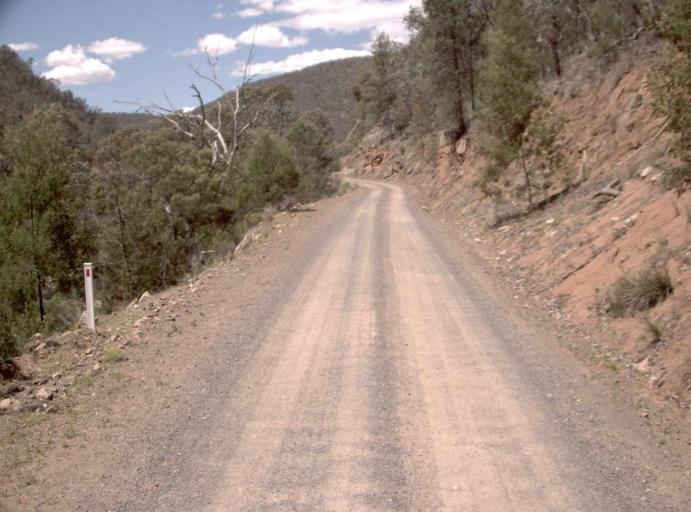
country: AU
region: New South Wales
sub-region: Snowy River
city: Jindabyne
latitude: -37.0612
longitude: 148.5238
